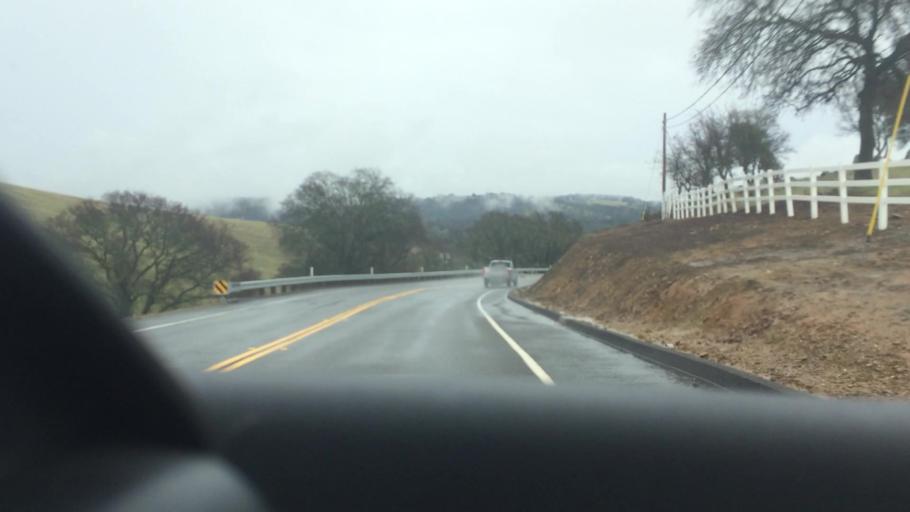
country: US
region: California
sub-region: El Dorado County
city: Cameron Park
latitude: 38.6060
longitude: -121.0317
